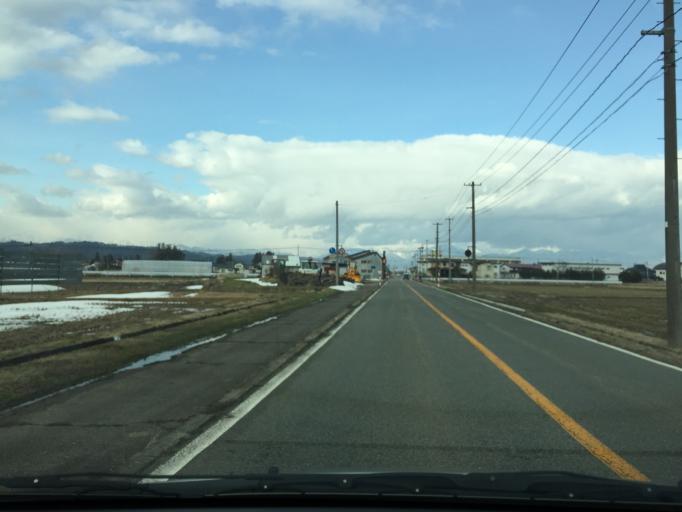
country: JP
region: Fukushima
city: Kitakata
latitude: 37.5840
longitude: 139.8346
